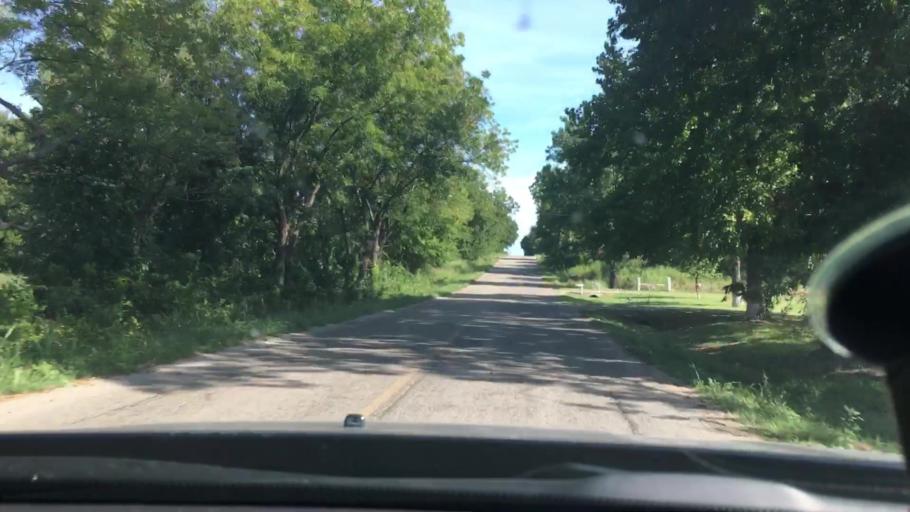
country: US
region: Oklahoma
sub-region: Carter County
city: Lone Grove
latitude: 34.2903
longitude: -97.2824
